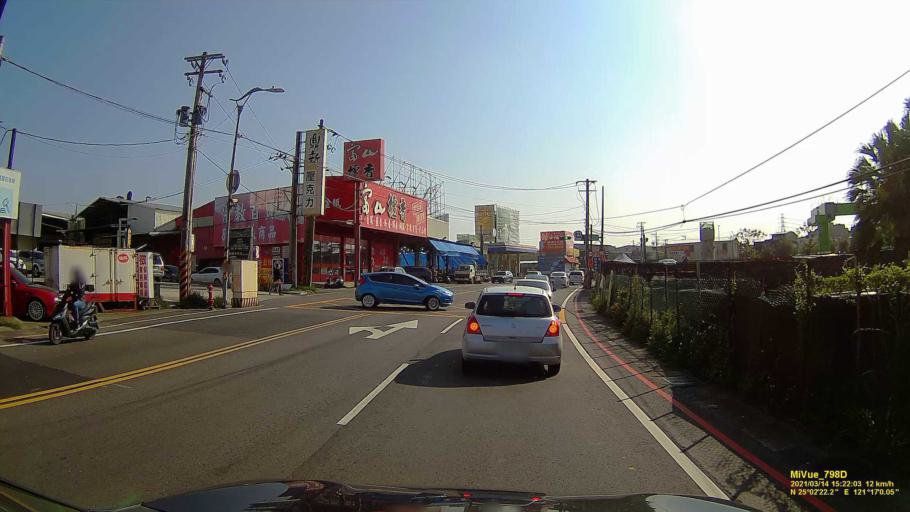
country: TW
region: Taiwan
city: Taoyuan City
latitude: 25.0394
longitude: 121.2833
